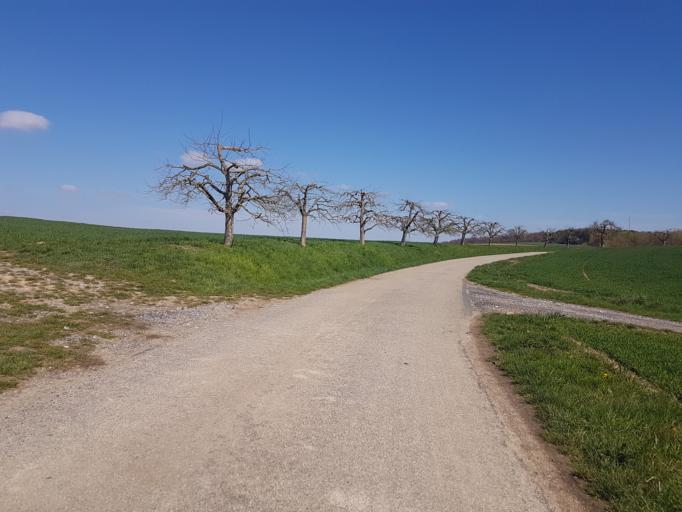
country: DE
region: Baden-Wuerttemberg
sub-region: Regierungsbezirk Stuttgart
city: Jagsthausen
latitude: 49.3602
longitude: 9.4961
